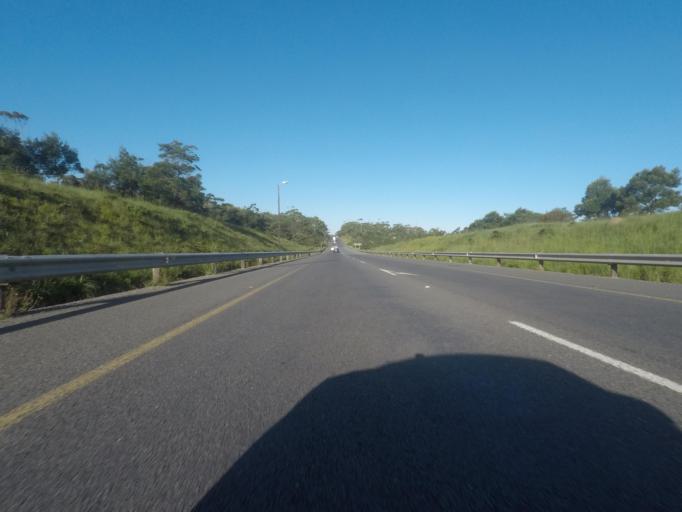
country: ZA
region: Eastern Cape
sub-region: Buffalo City Metropolitan Municipality
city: East London
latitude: -33.0481
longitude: 27.8196
